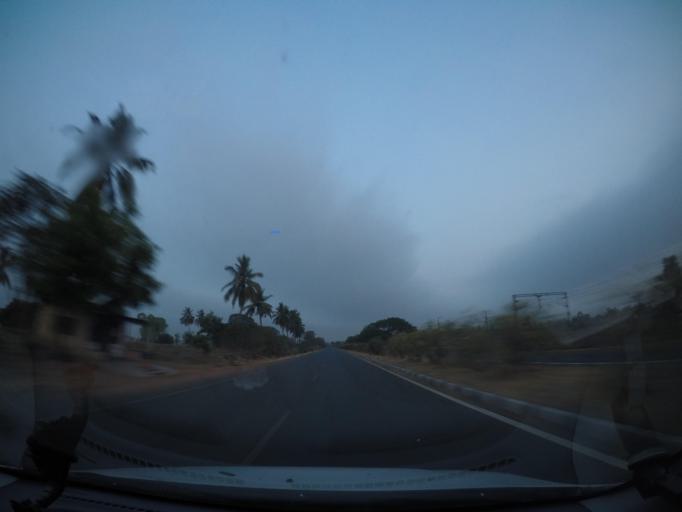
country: IN
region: Andhra Pradesh
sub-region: West Godavari
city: Tadepallegudem
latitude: 16.8183
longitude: 81.3914
